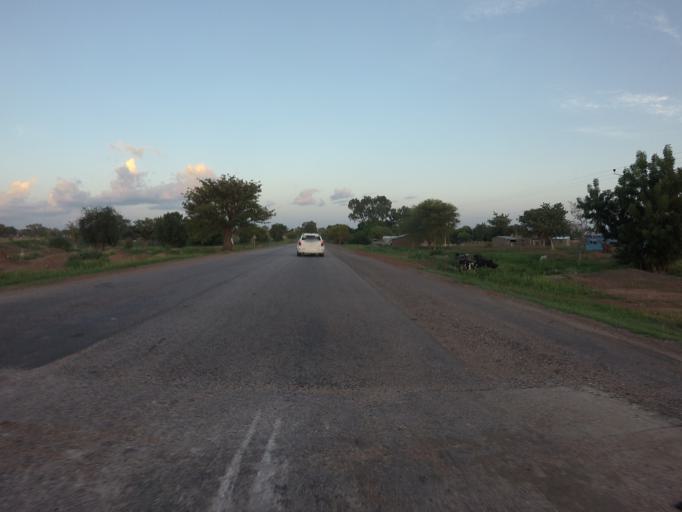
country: GH
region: Upper East
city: Navrongo
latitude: 10.8644
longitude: -1.0367
